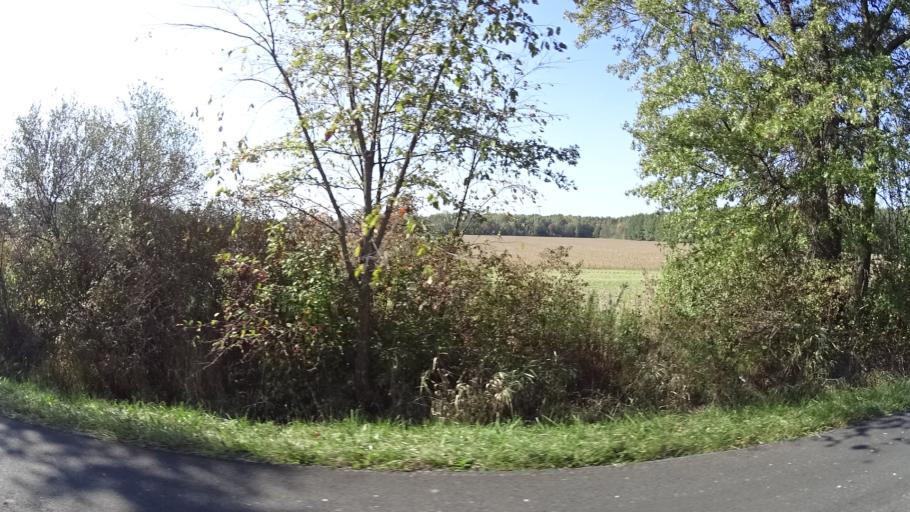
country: US
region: Ohio
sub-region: Lorain County
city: Vermilion-on-the-Lake
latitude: 41.4062
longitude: -82.3043
